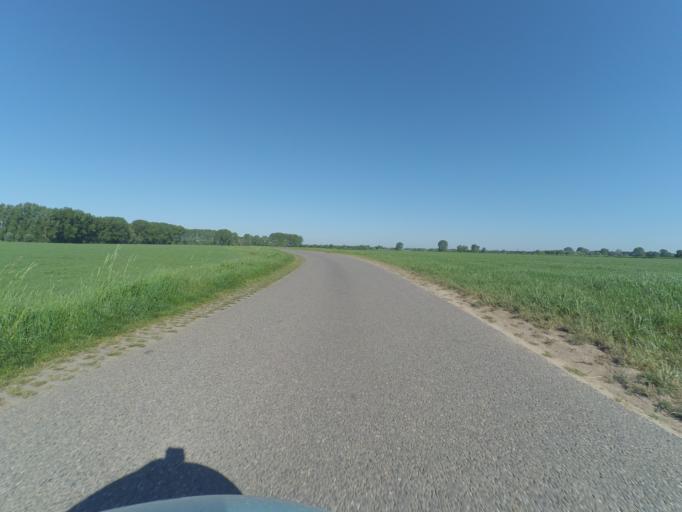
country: NL
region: Gelderland
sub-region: Gemeente Lochem
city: Epse
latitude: 52.2143
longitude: 6.1768
